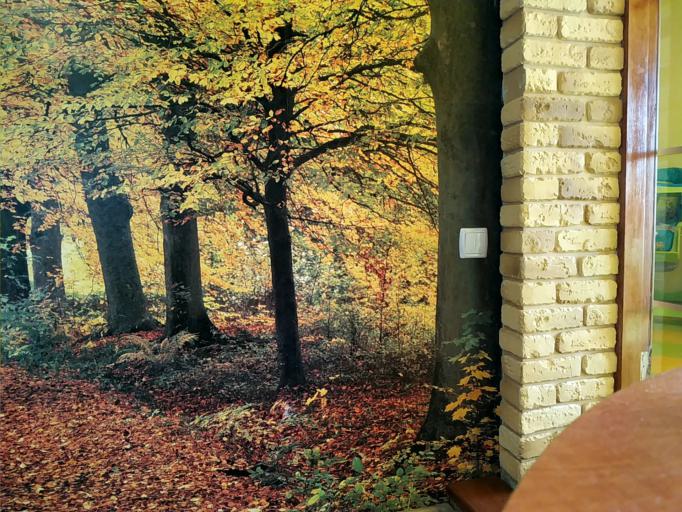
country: RU
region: Novgorod
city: Staraya Russa
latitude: 57.8336
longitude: 31.4806
